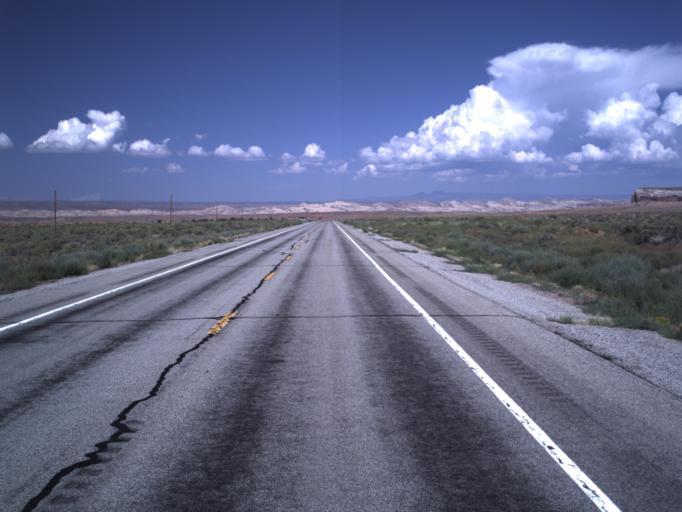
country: US
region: Utah
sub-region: San Juan County
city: Blanding
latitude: 37.1937
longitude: -109.5983
